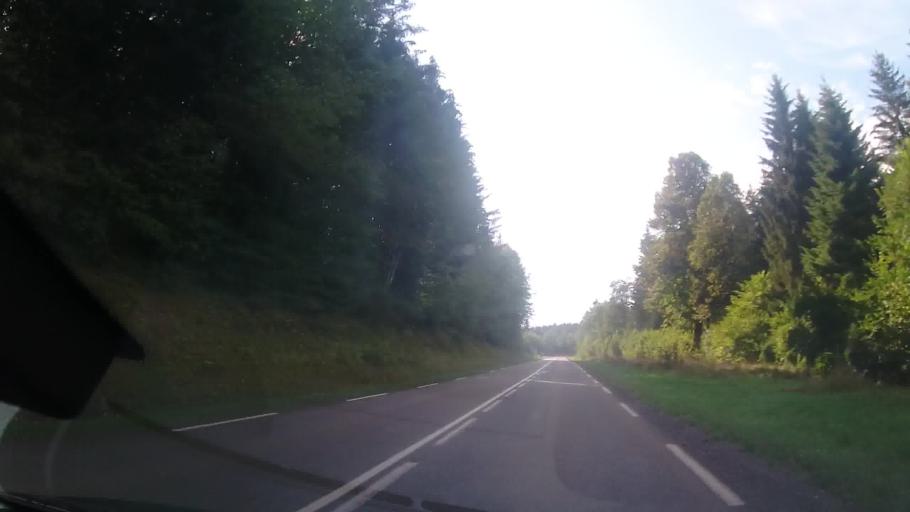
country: FR
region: Franche-Comte
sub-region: Departement du Jura
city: Clairvaux-les-Lacs
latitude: 46.5834
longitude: 5.8125
